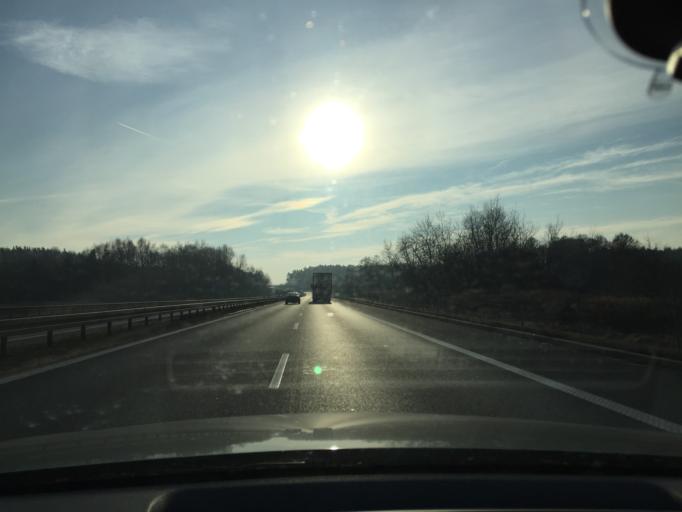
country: PL
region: Lesser Poland Voivodeship
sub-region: Powiat krakowski
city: Kryspinow
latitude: 50.0521
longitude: 19.8090
